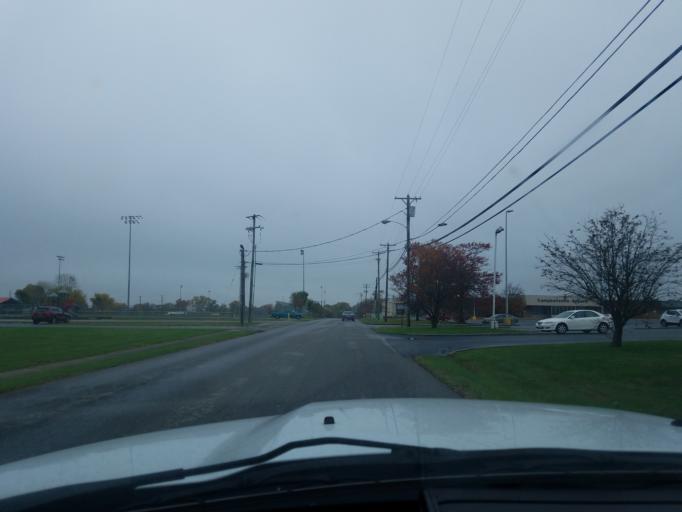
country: US
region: Kentucky
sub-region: Taylor County
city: Campbellsville
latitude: 37.3514
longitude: -85.3323
